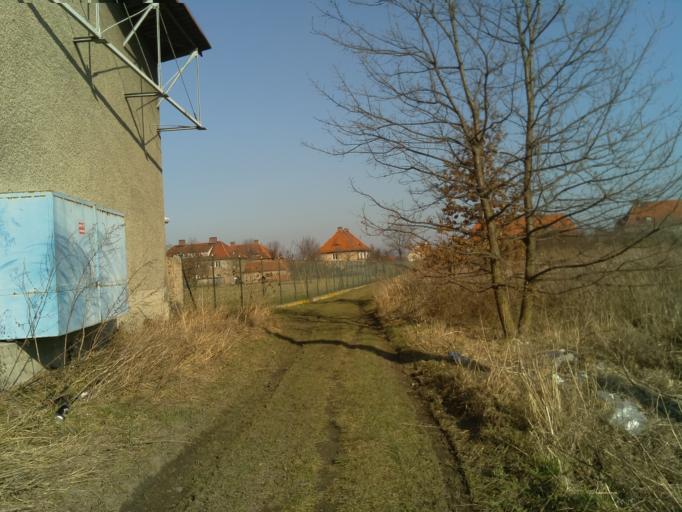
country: PL
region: Lower Silesian Voivodeship
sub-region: Powiat swidnicki
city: Swiebodzice
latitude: 50.8700
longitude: 16.3382
